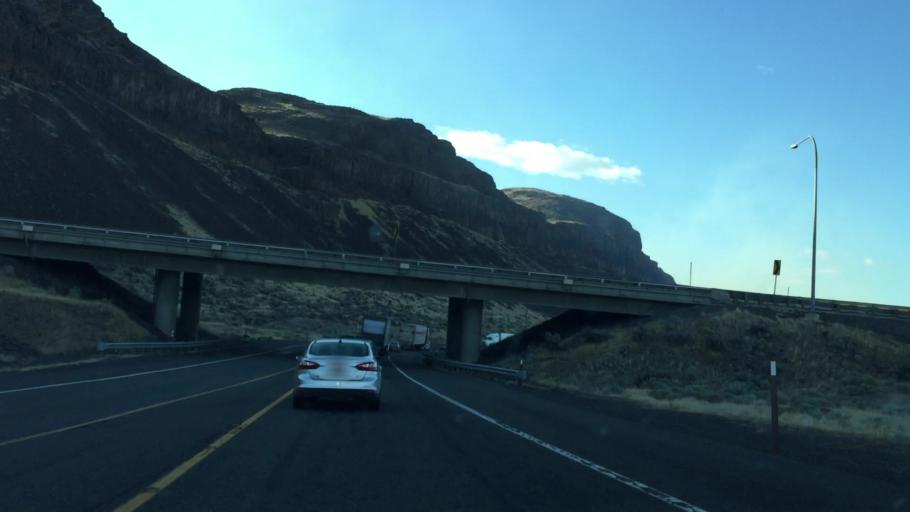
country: US
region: Washington
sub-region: Grant County
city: Mattawa
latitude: 46.9455
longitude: -119.9625
